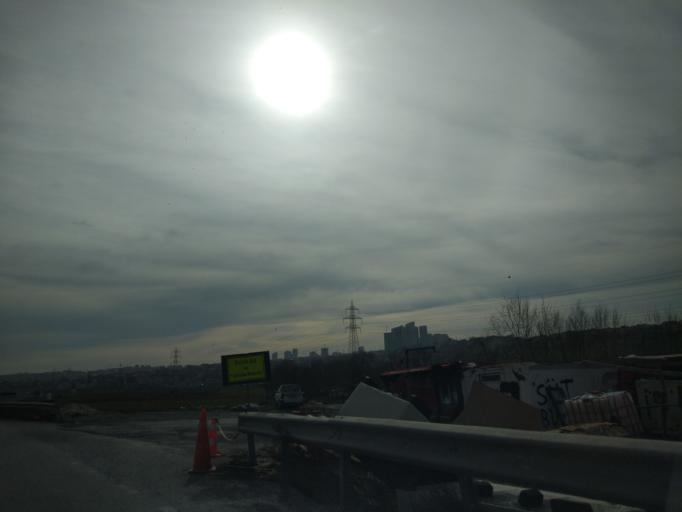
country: TR
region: Istanbul
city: Esenyurt
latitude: 41.0529
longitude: 28.7023
